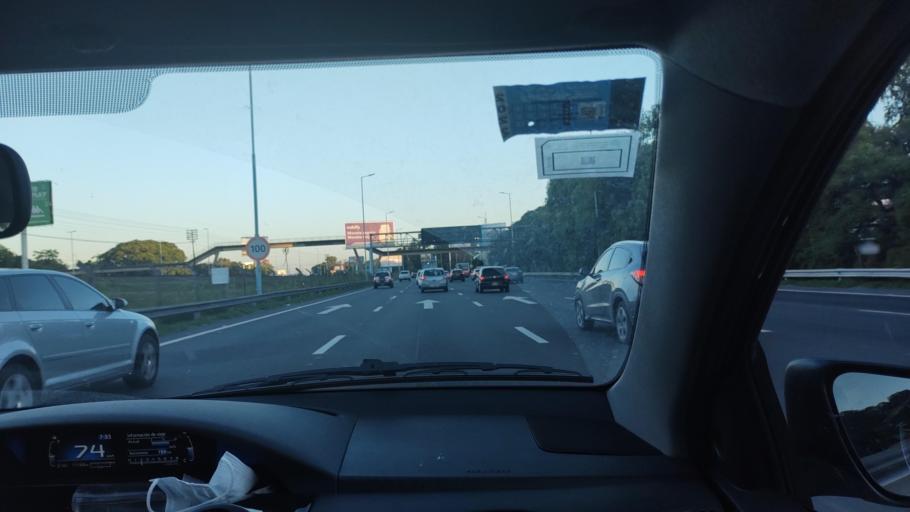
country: AR
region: Buenos Aires F.D.
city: Colegiales
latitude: -34.5366
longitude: -58.4610
